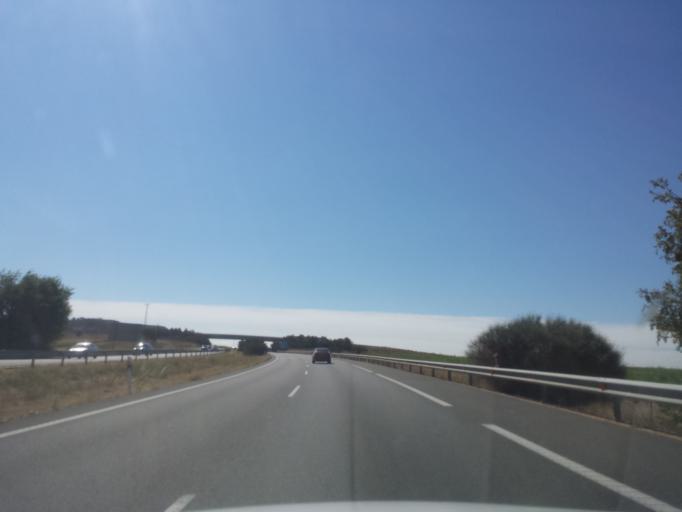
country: ES
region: Castille and Leon
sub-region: Provincia de Valladolid
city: Vega de Valdetronco
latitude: 41.5842
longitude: -5.1100
